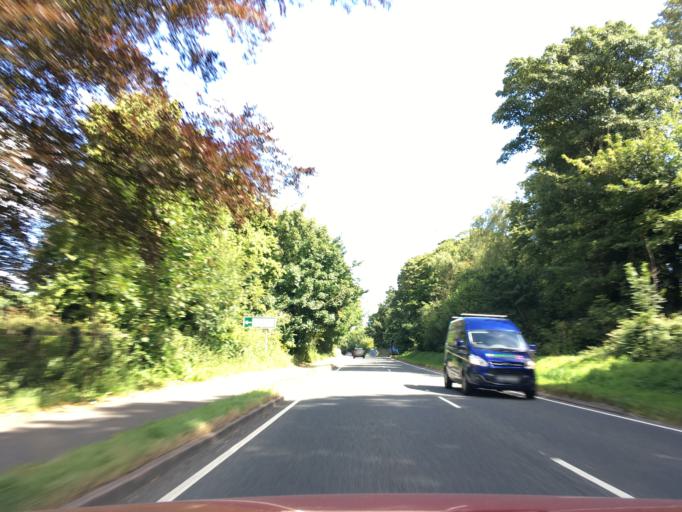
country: GB
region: England
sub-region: Dorset
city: Dorchester
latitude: 50.7365
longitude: -2.4734
